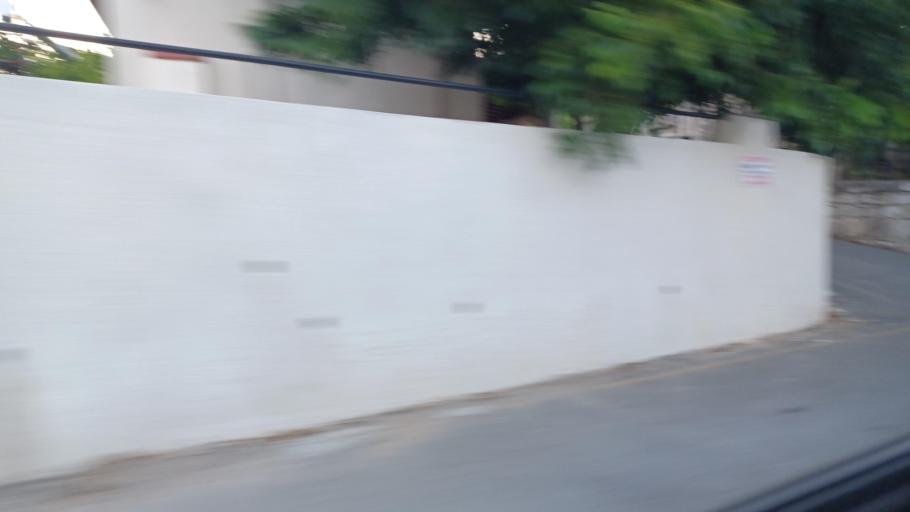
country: CY
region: Pafos
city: Mesogi
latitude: 34.8231
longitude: 32.5831
